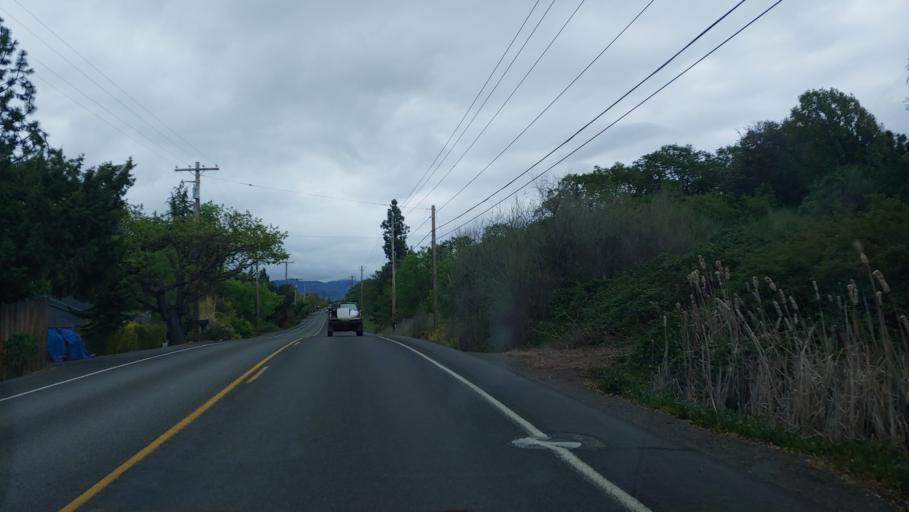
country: US
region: Oregon
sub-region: Jackson County
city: Ashland
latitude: 42.1891
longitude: -122.6626
